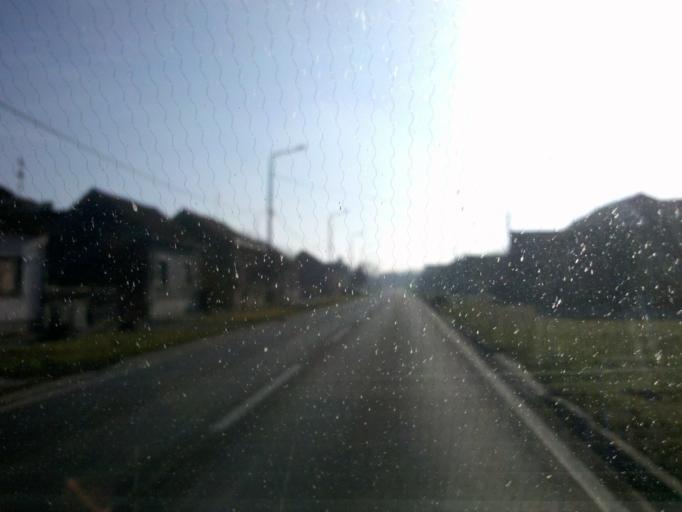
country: HR
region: Koprivnicko-Krizevacka
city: Virje
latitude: 46.0830
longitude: 16.9511
